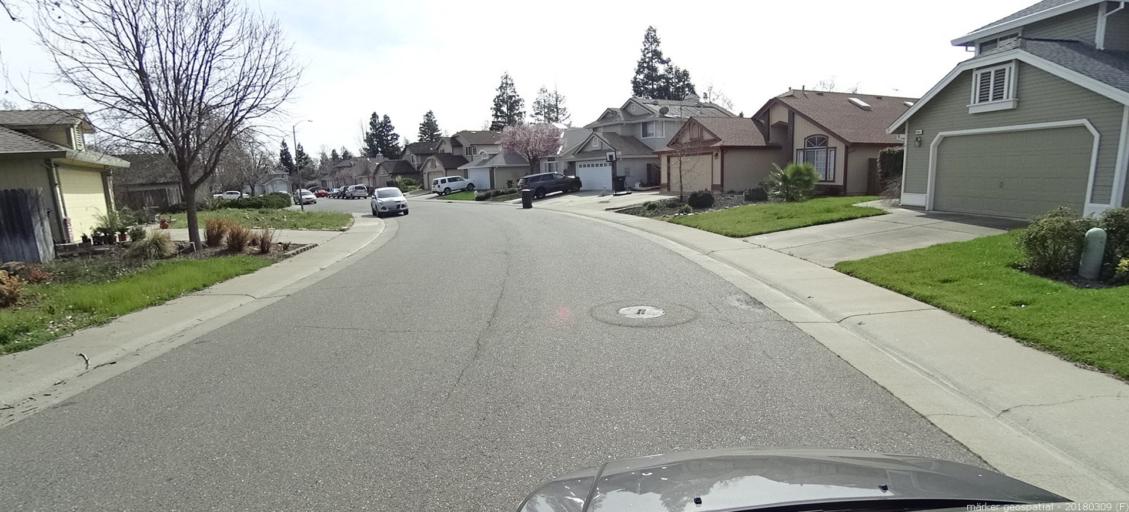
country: US
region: California
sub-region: Sacramento County
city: Florin
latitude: 38.4545
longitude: -121.3934
